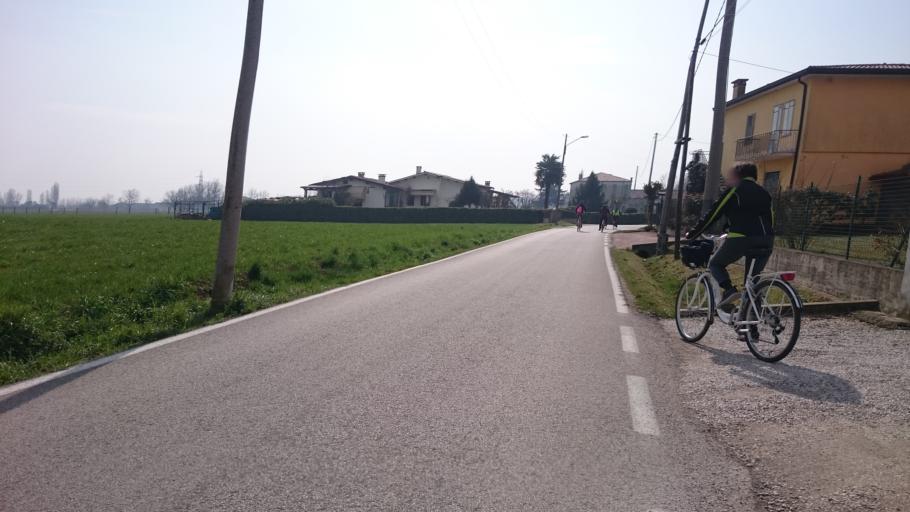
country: IT
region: Veneto
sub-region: Provincia di Vicenza
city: Villaganzerla
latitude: 45.4492
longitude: 11.6207
